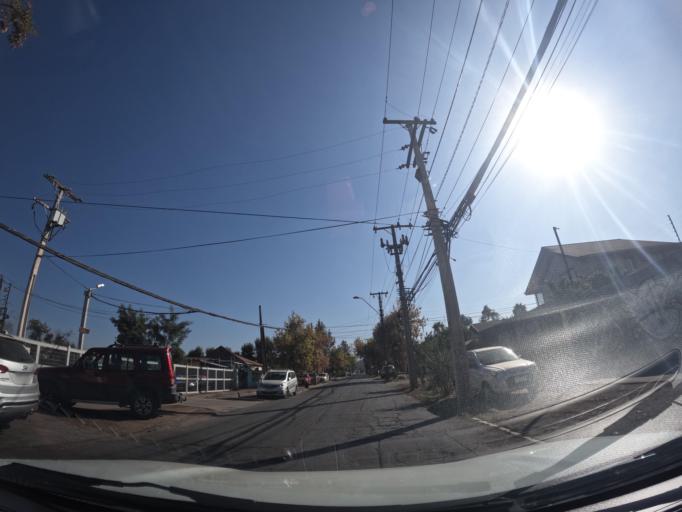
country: CL
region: Santiago Metropolitan
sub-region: Provincia de Santiago
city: Villa Presidente Frei, Nunoa, Santiago, Chile
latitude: -33.4670
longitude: -70.5741
